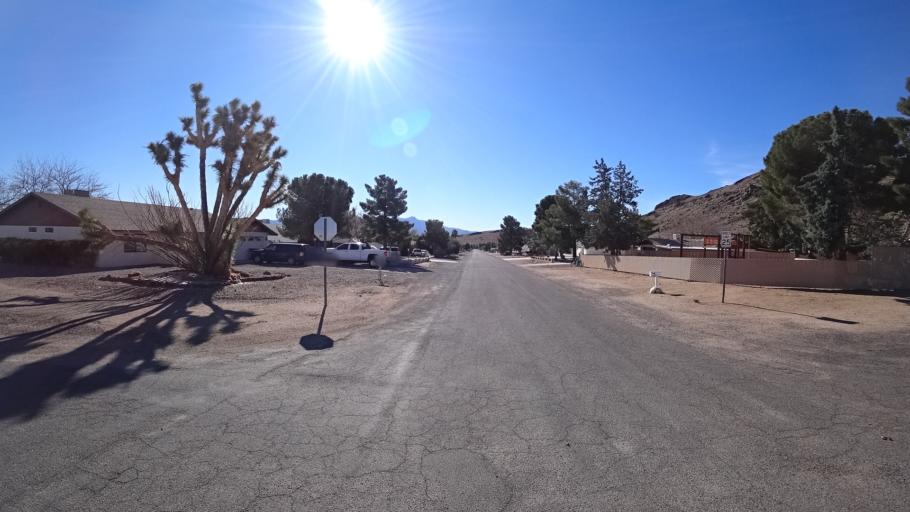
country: US
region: Arizona
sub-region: Mohave County
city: New Kingman-Butler
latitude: 35.2663
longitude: -114.0480
